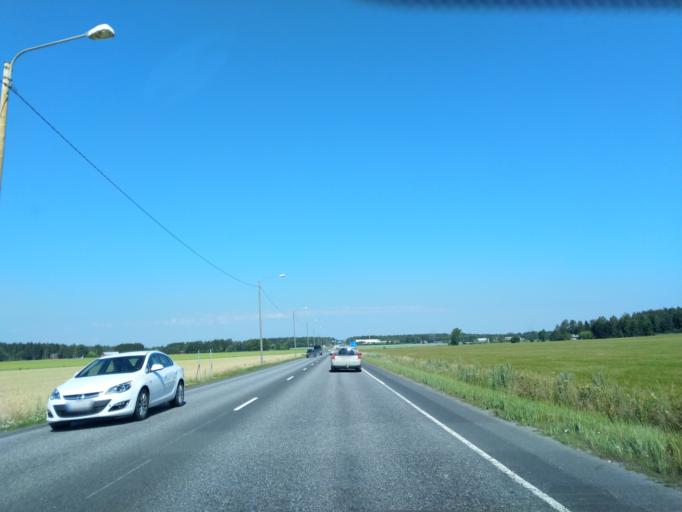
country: FI
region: Satakunta
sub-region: Pori
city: Nakkila
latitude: 61.3708
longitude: 21.9795
